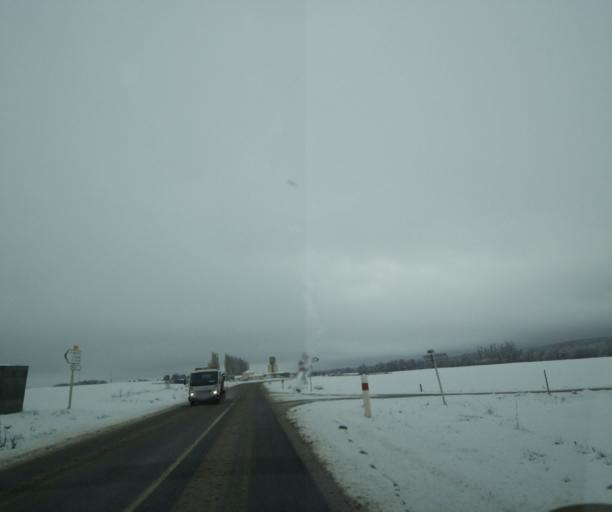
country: FR
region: Champagne-Ardenne
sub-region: Departement de la Haute-Marne
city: Wassy
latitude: 48.5174
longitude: 4.9353
